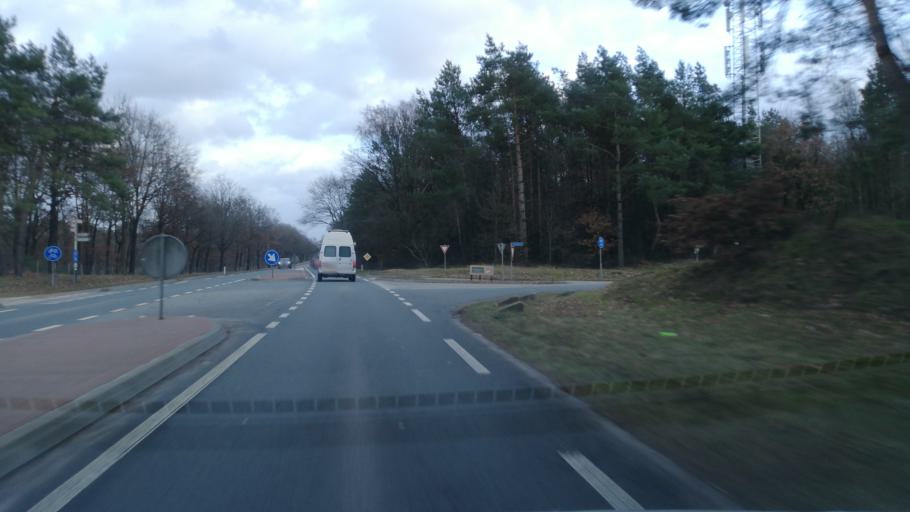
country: NL
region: Gelderland
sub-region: Gemeente Barneveld
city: Garderen
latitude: 52.2809
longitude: 5.7033
